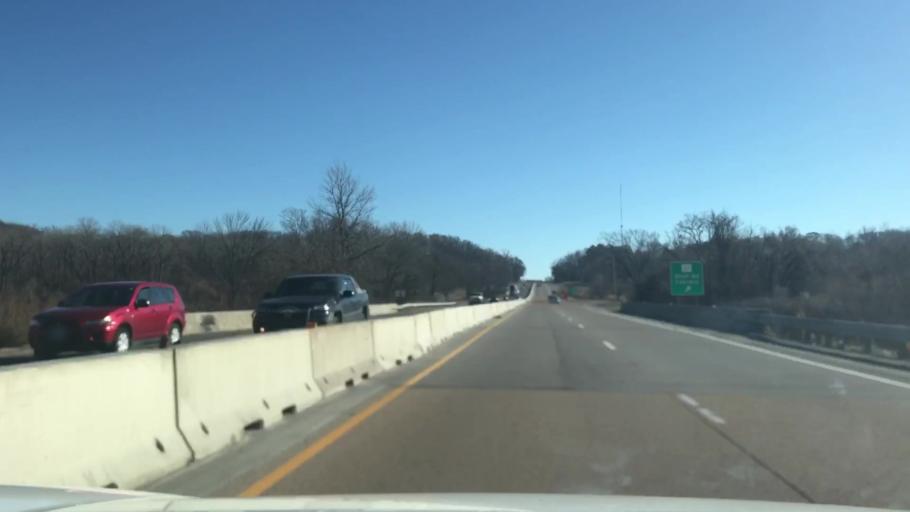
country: US
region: Illinois
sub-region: Saint Clair County
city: Alorton
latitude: 38.5703
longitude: -90.0943
